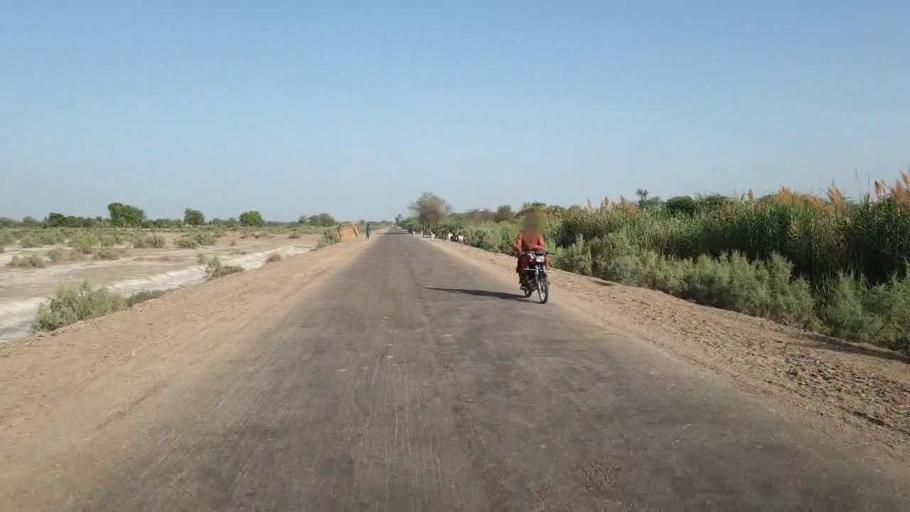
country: PK
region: Sindh
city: Nawabshah
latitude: 26.3884
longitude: 68.4517
